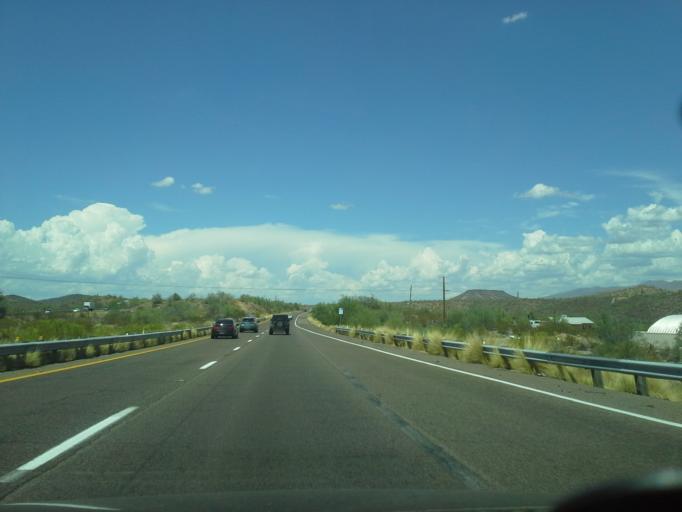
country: US
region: Arizona
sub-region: Maricopa County
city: New River
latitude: 33.9191
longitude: -112.1443
